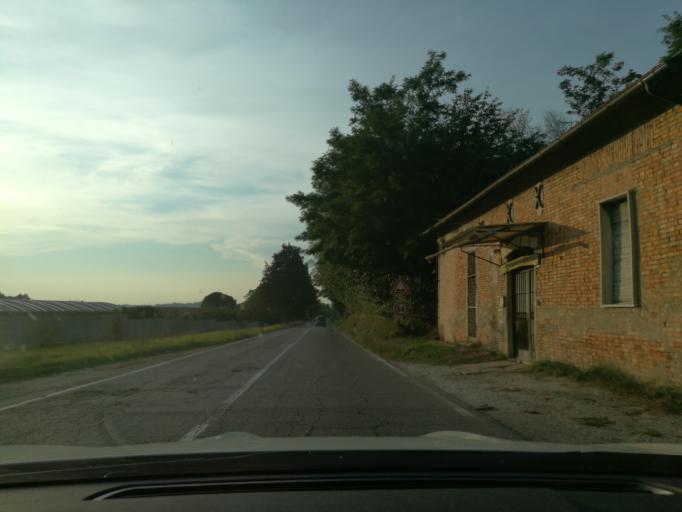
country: IT
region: Umbria
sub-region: Provincia di Terni
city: San Gemini
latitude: 42.6335
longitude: 12.5512
